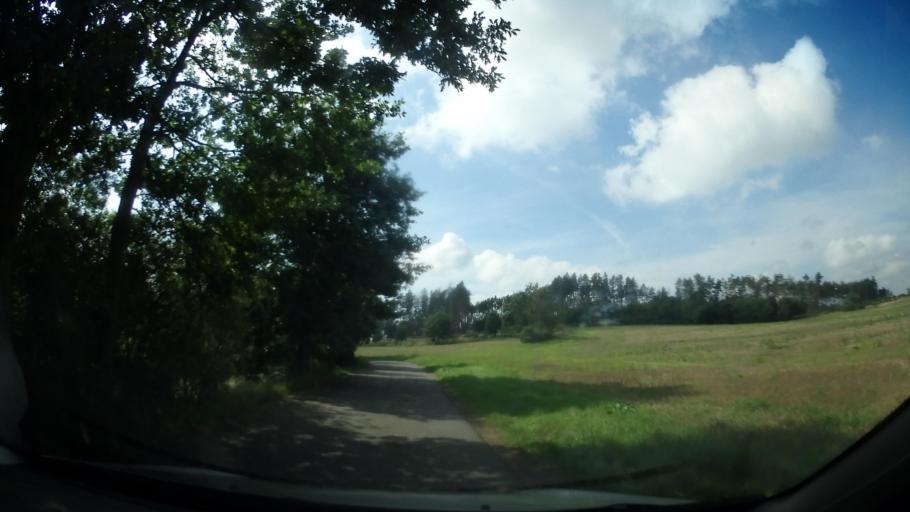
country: CZ
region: Central Bohemia
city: Novy Knin
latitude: 49.6933
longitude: 14.3237
